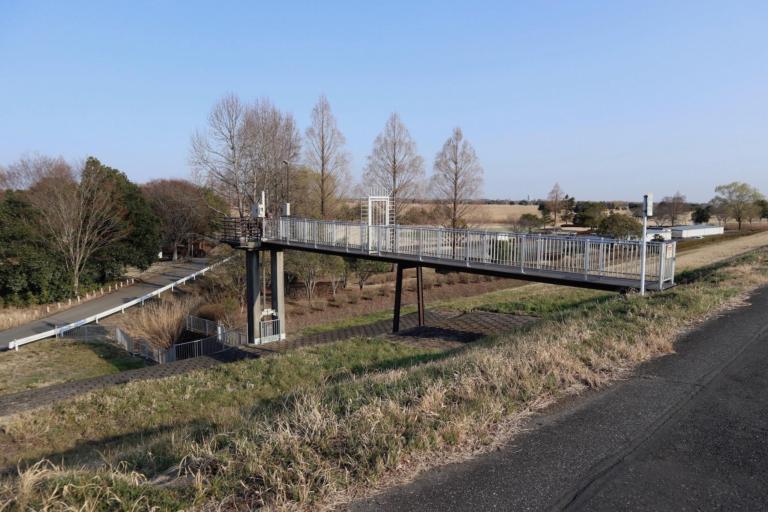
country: JP
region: Tochigi
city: Fujioka
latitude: 36.2501
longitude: 139.6533
